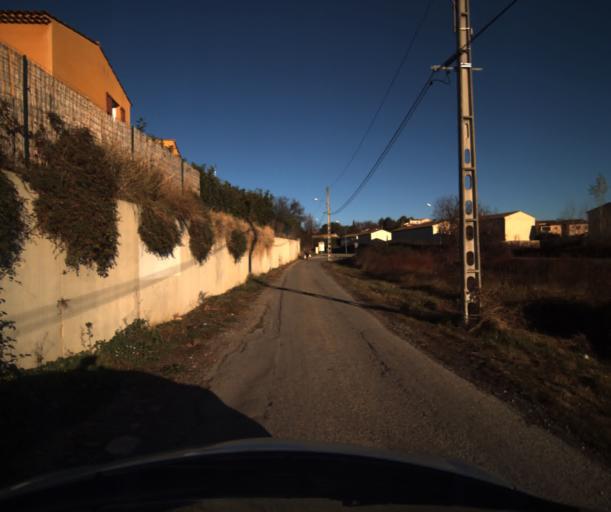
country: FR
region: Provence-Alpes-Cote d'Azur
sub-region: Departement du Vaucluse
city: Pertuis
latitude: 43.7014
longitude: 5.4985
